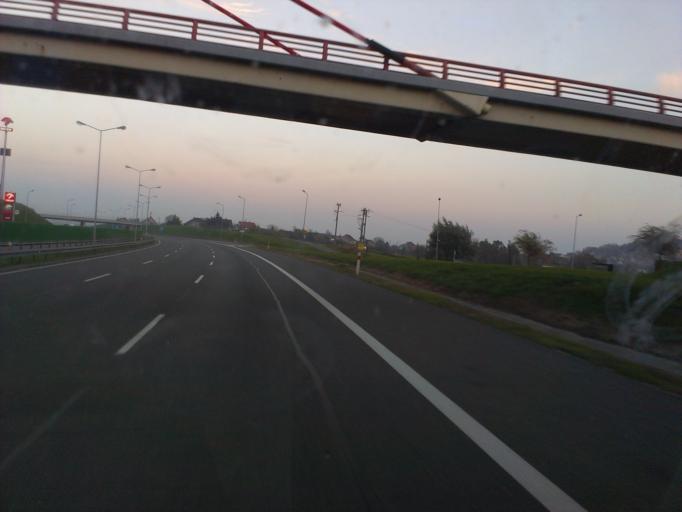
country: PL
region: Opole Voivodeship
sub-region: Powiat strzelecki
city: Lesnica
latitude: 50.4619
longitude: 18.1610
